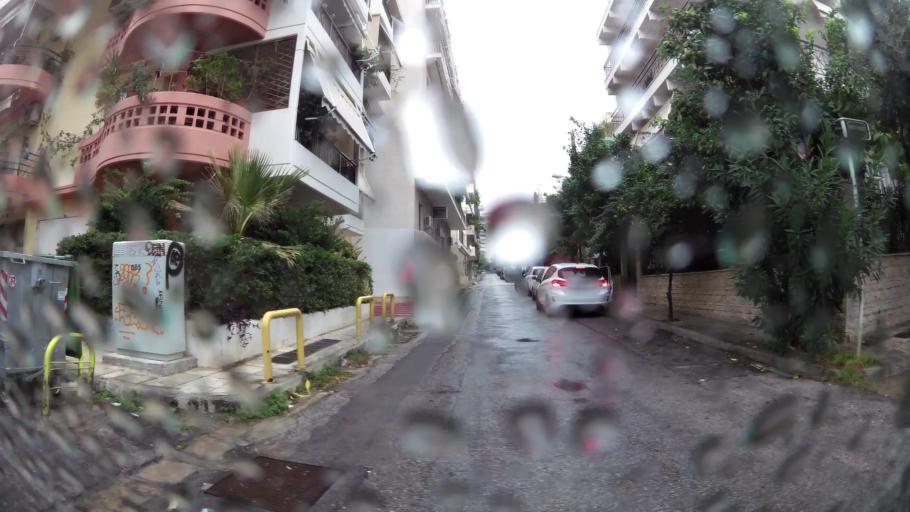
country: GR
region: Attica
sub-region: Nomarchia Athinas
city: Ymittos
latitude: 37.9560
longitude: 23.7420
